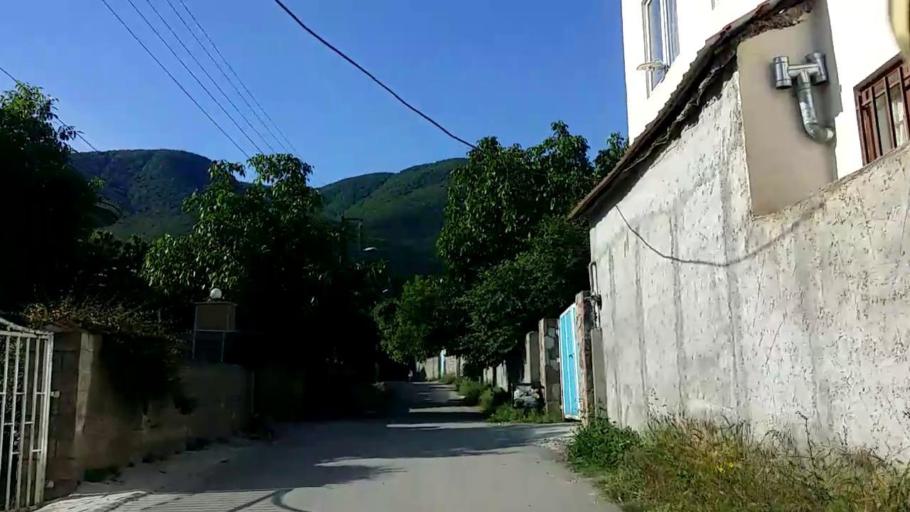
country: IR
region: Mazandaran
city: `Abbasabad
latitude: 36.5028
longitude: 51.1568
